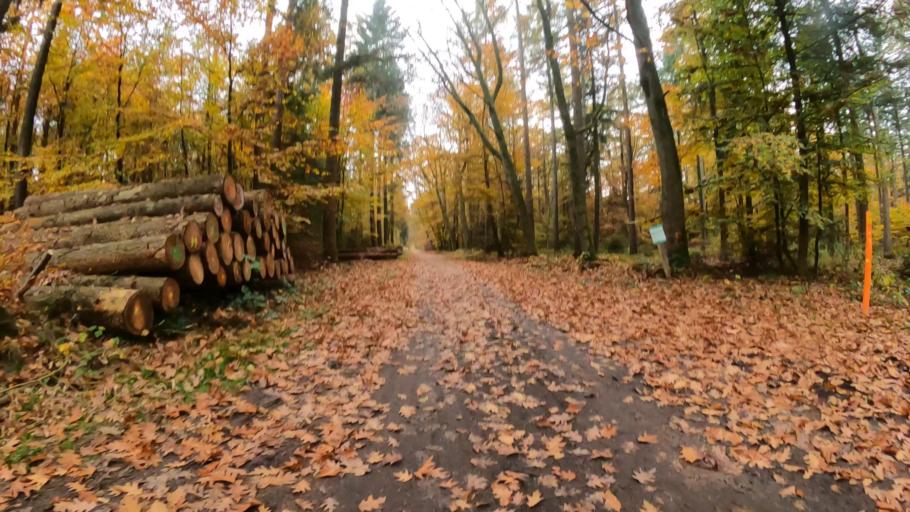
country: DE
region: Lower Saxony
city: Buchholz in der Nordheide
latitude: 53.3703
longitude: 9.8249
